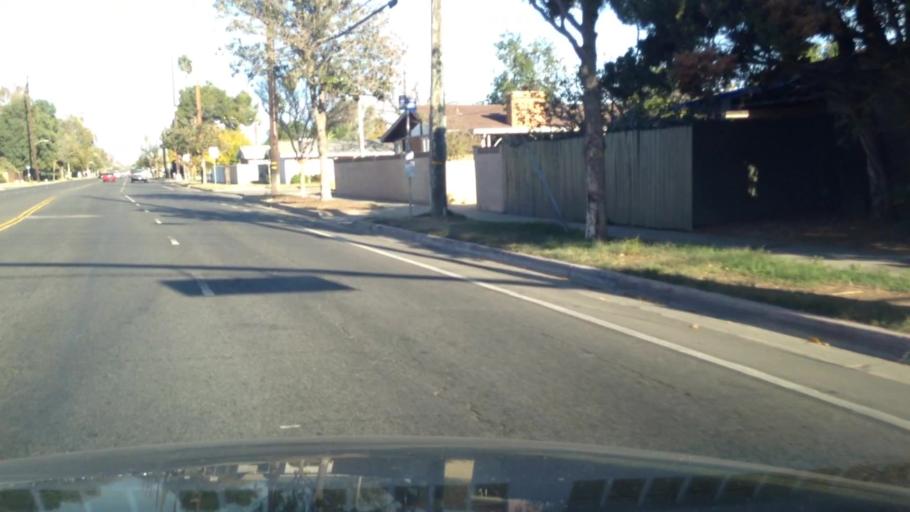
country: US
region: California
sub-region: Riverside County
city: Riverside
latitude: 33.9309
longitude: -117.4440
